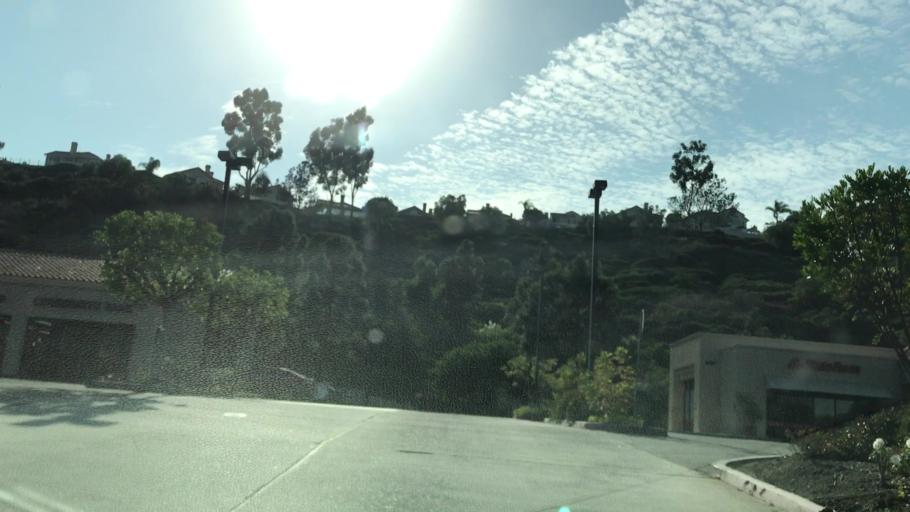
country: US
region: California
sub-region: Orange County
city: Laguna Niguel
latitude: 33.5076
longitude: -117.7083
